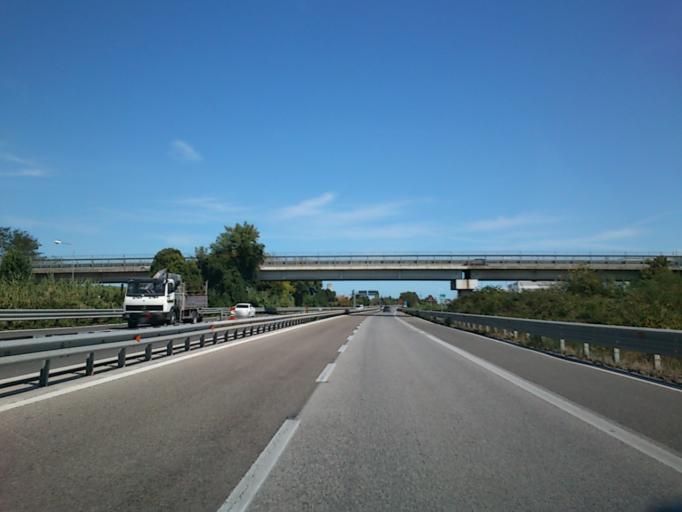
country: IT
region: The Marches
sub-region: Provincia di Pesaro e Urbino
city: Bellocchi
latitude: 43.7885
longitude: 12.9958
